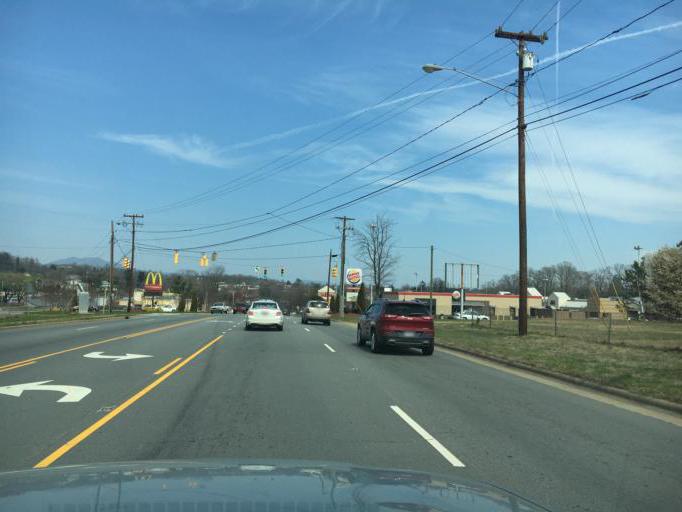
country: US
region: North Carolina
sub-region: McDowell County
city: Marion
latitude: 35.6746
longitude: -82.0143
